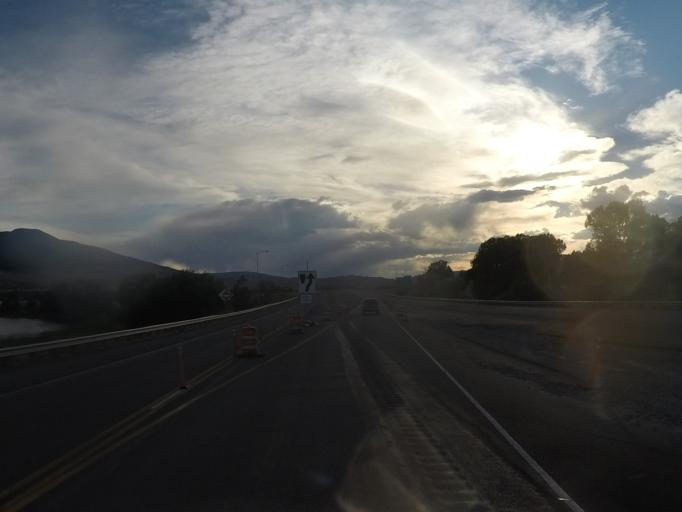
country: US
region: Montana
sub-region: Park County
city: Livingston
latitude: 45.6444
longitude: -110.5643
